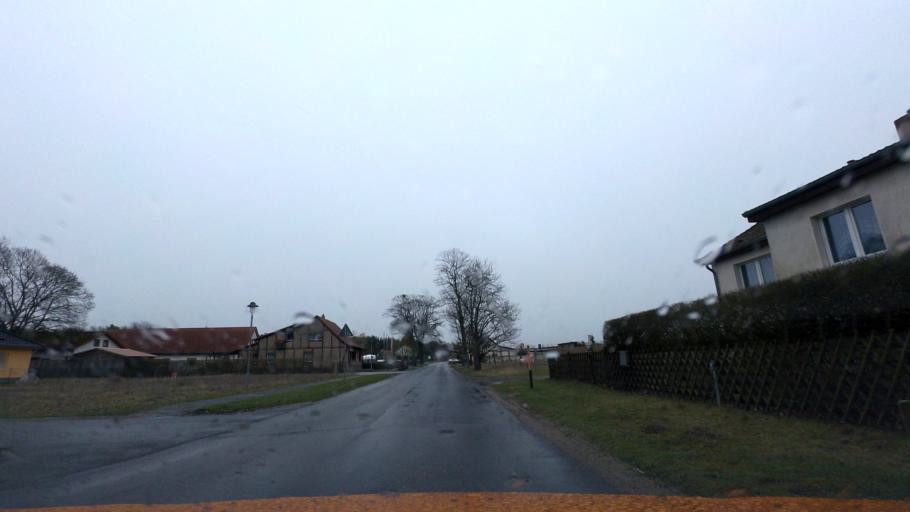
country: DE
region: Brandenburg
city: Brieselang
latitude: 52.6520
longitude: 12.9919
